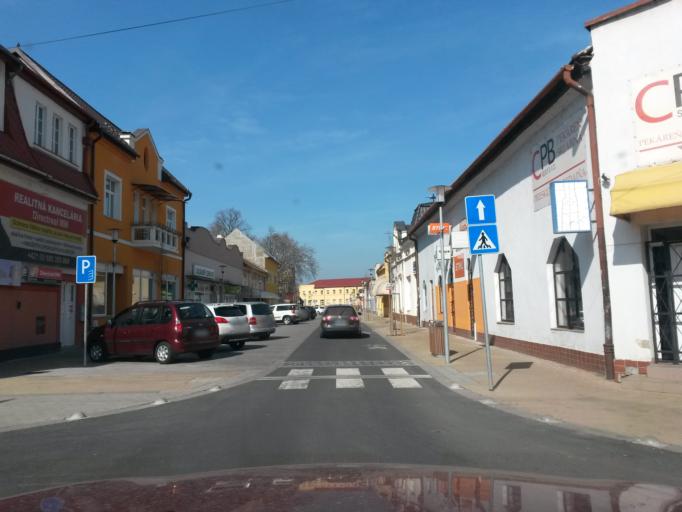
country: SK
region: Banskobystricky
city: Lucenec
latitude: 48.3341
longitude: 19.6668
